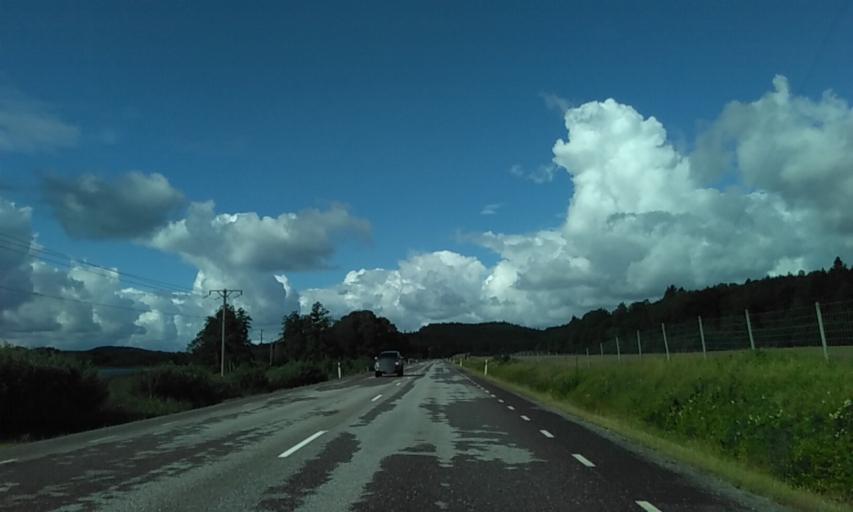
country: SE
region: Vaestra Goetaland
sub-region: Alingsas Kommun
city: Alingsas
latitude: 57.9671
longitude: 12.4146
